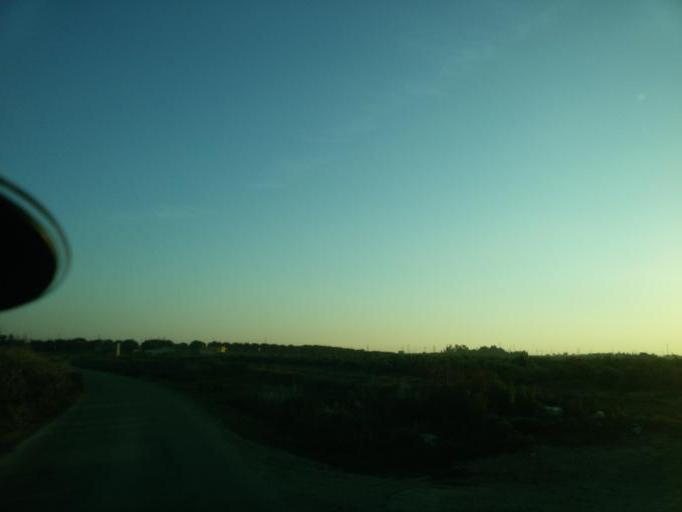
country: IT
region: Apulia
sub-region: Provincia di Brindisi
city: La Rosa
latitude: 40.6158
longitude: 17.9403
